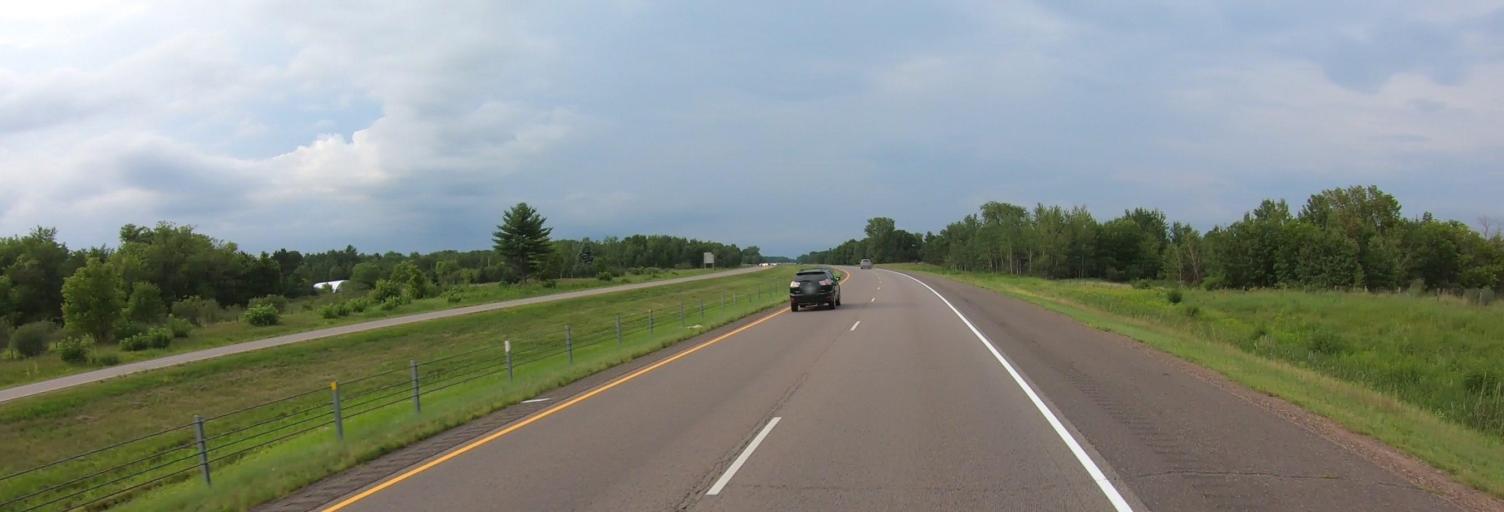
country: US
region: Minnesota
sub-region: Chisago County
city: Stacy
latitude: 45.4126
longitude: -92.9881
